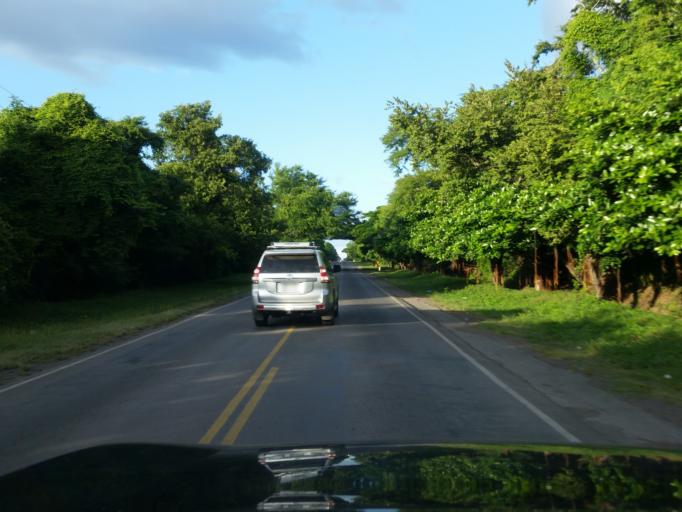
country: NI
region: Granada
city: Nandaime
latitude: 11.7953
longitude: -86.0479
